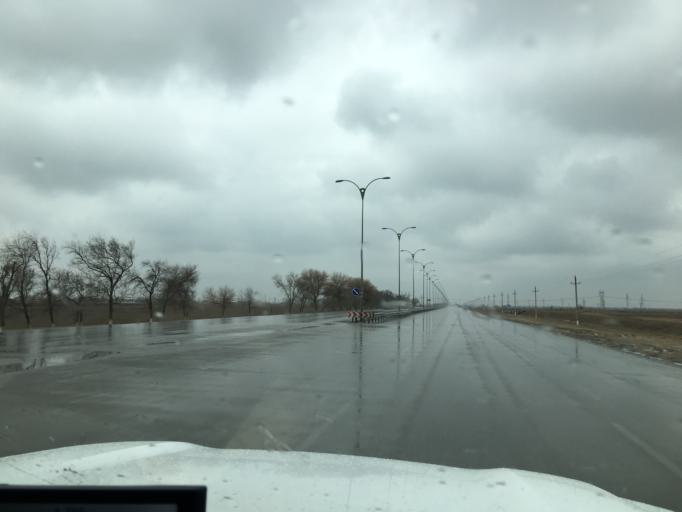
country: TM
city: Murgab
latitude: 37.5175
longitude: 61.9236
